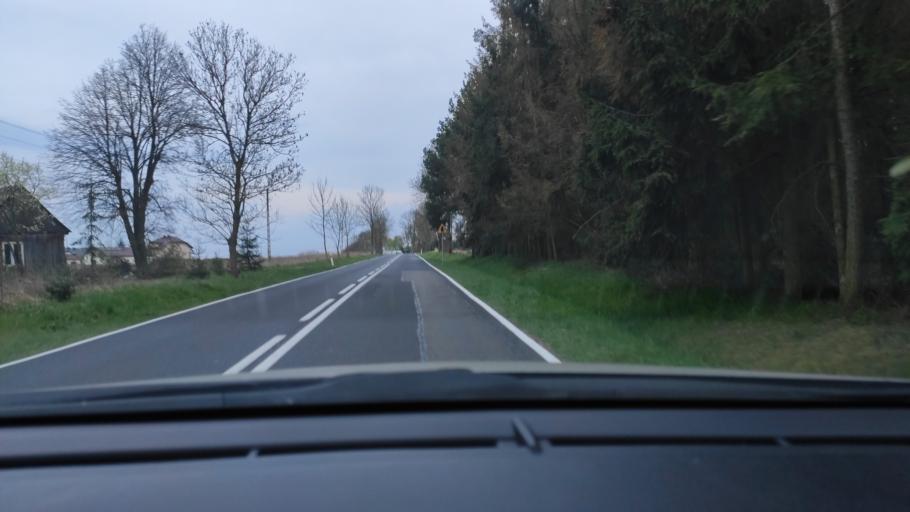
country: PL
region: Masovian Voivodeship
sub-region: Powiat zwolenski
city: Zwolen
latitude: 51.3854
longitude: 21.5550
